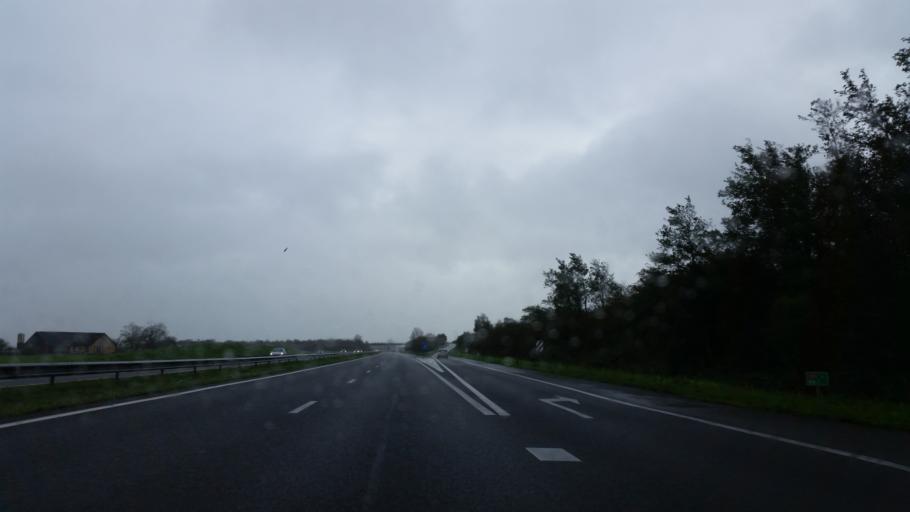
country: NL
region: Friesland
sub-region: Gemeente Boarnsterhim
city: Reduzum
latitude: 53.1172
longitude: 5.8099
